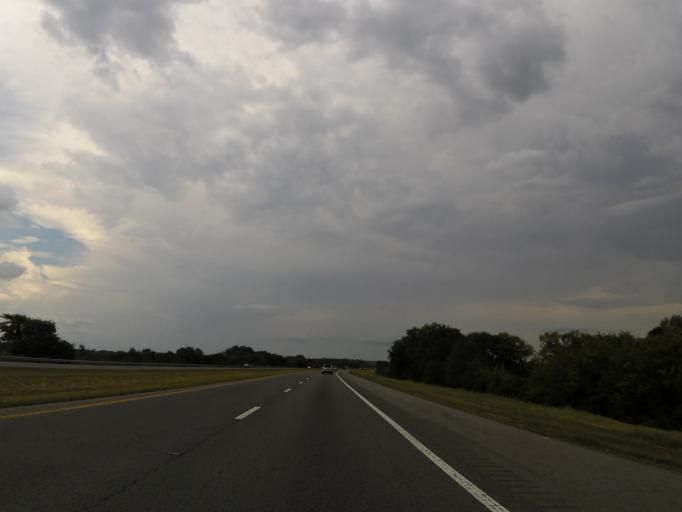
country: US
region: Tennessee
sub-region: Rutherford County
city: Smyrna
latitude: 36.0010
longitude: -86.4296
